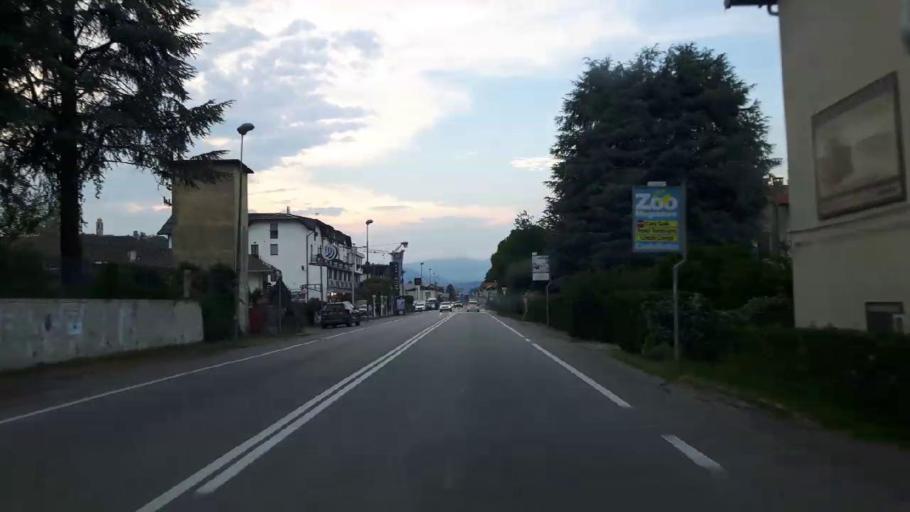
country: IT
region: Piedmont
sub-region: Provincia di Novara
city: Dormelletto
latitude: 45.7287
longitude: 8.5786
